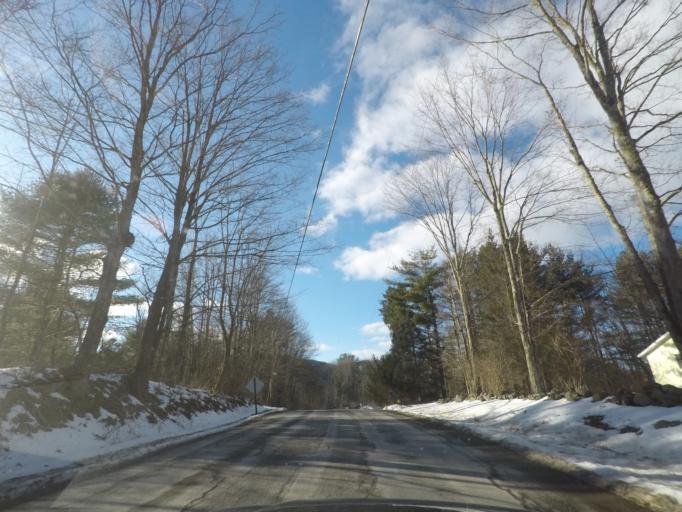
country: US
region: New York
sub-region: Rensselaer County
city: Nassau
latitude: 42.5186
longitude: -73.5219
